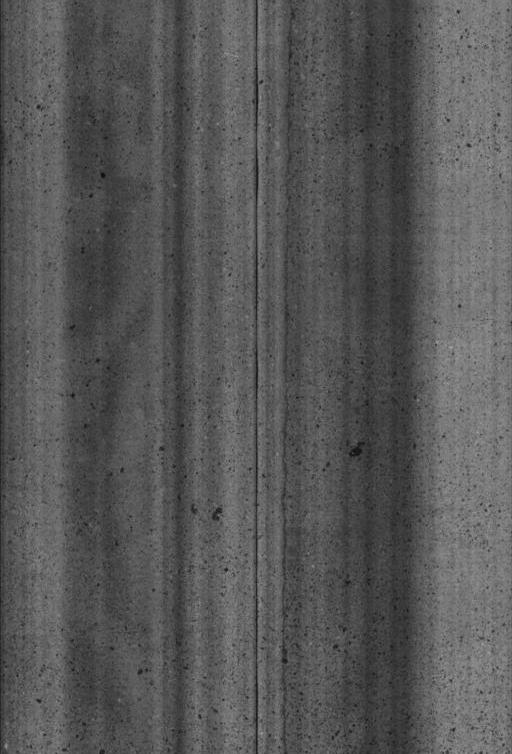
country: US
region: Maryland
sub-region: Montgomery County
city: Takoma Park
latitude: 38.9699
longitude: -77.0177
